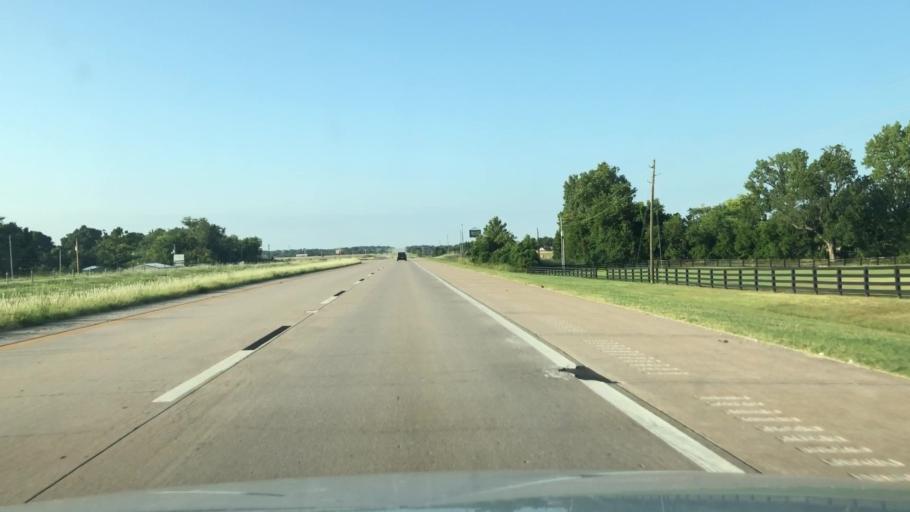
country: US
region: Oklahoma
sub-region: Osage County
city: Skiatook
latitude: 36.4618
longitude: -95.9207
